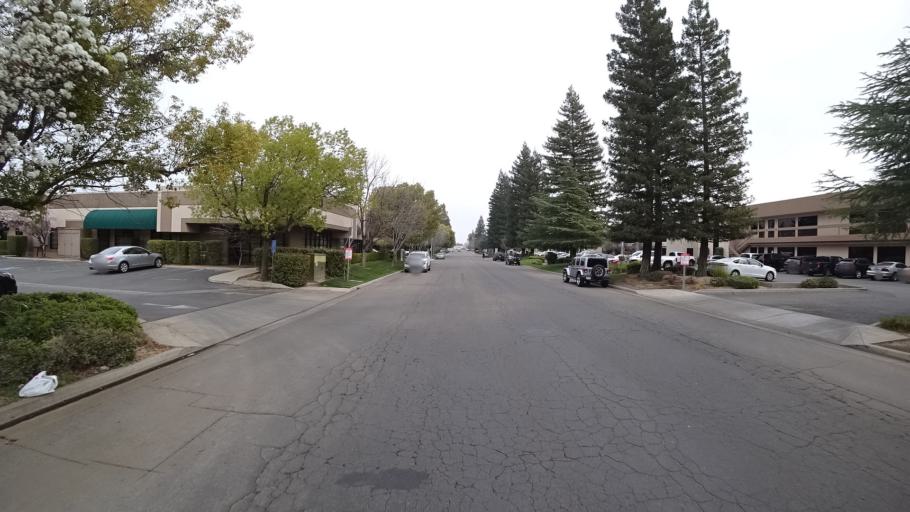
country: US
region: California
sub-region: Fresno County
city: Clovis
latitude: 36.8494
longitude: -119.8004
